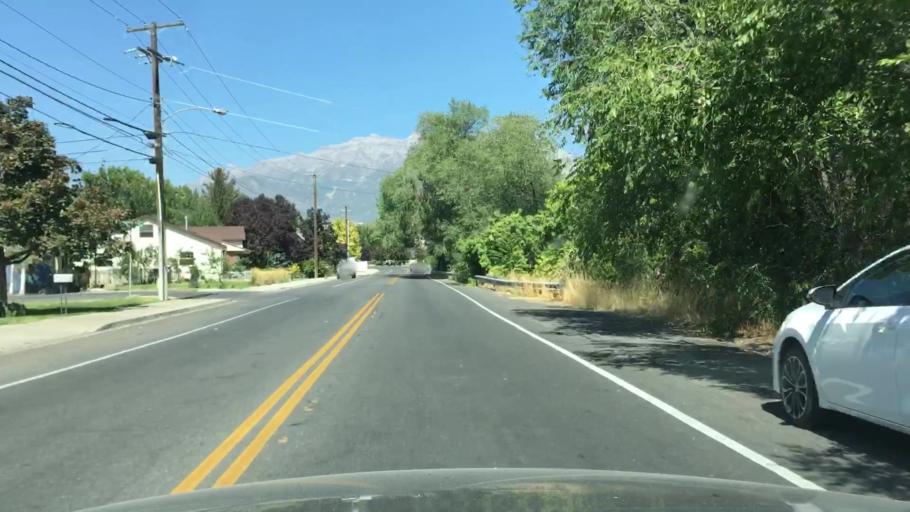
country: US
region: Utah
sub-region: Utah County
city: Provo
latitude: 40.2610
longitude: -111.6716
